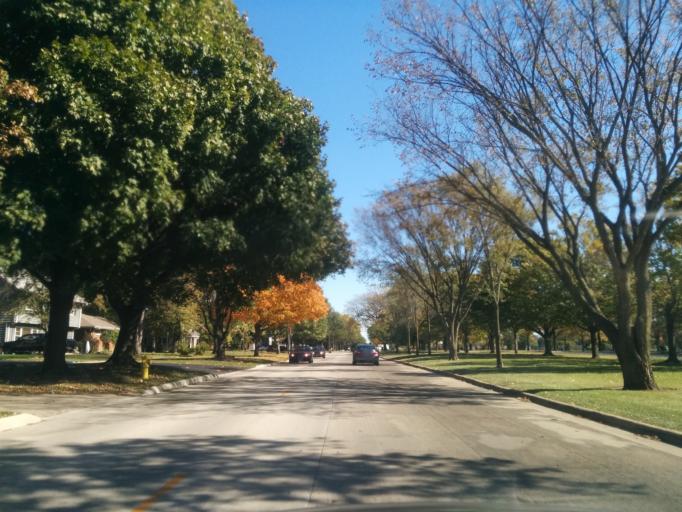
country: US
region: Illinois
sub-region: DuPage County
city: Lombard
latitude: 41.8752
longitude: -88.0004
